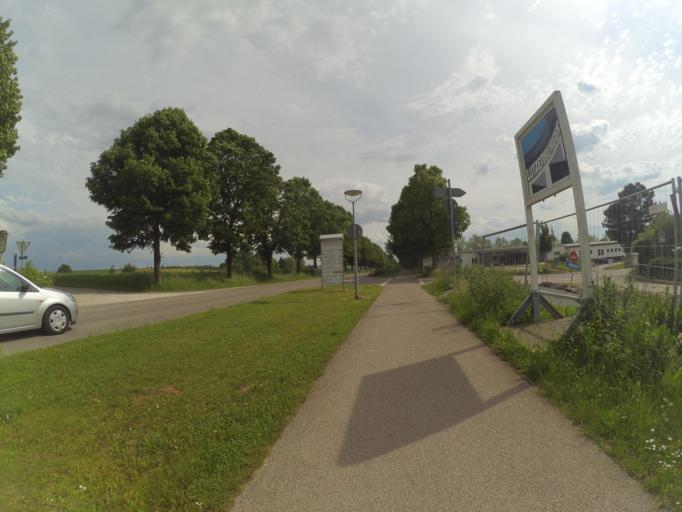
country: DE
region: Bavaria
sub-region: Swabia
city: Guenzburg
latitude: 48.4565
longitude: 10.2951
